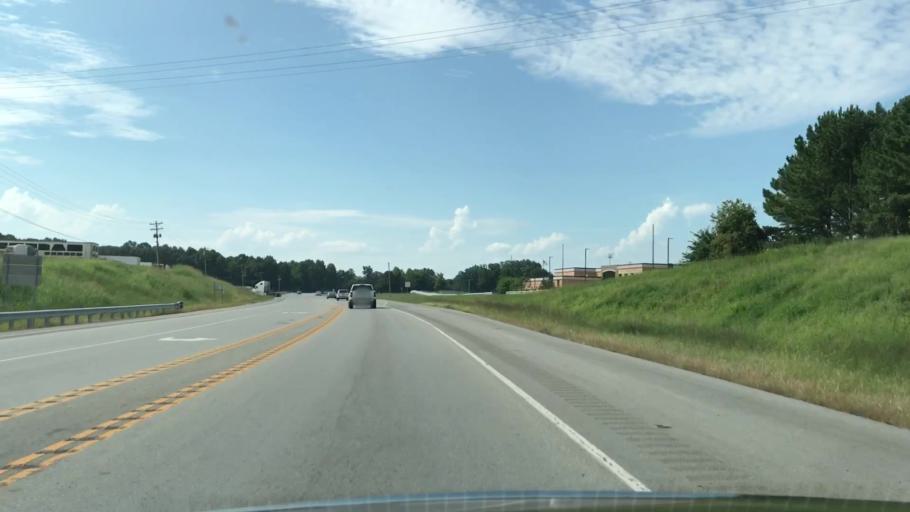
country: US
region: Kentucky
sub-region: Allen County
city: Scottsville
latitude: 36.7553
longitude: -86.2135
